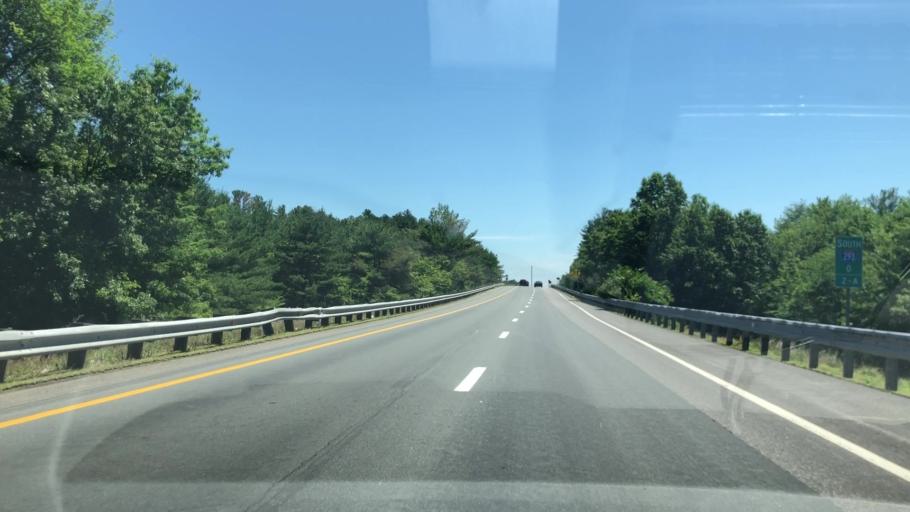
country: US
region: New Hampshire
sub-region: Hillsborough County
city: Manchester
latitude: 42.9593
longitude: -71.4110
